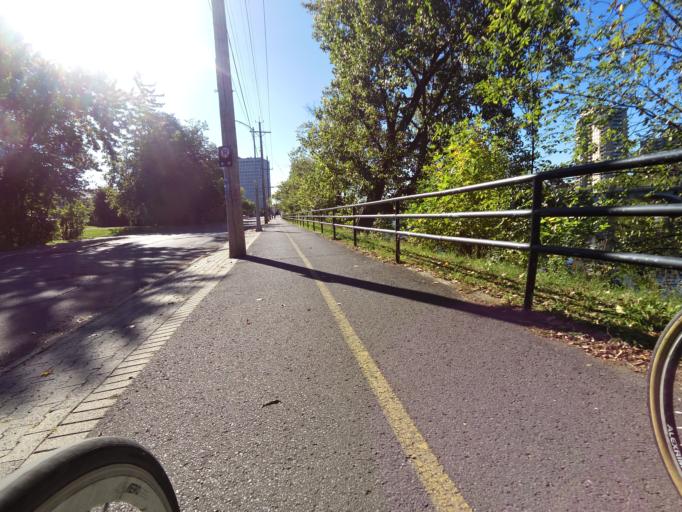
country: CA
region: Ontario
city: Ottawa
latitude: 45.4344
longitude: -75.6709
